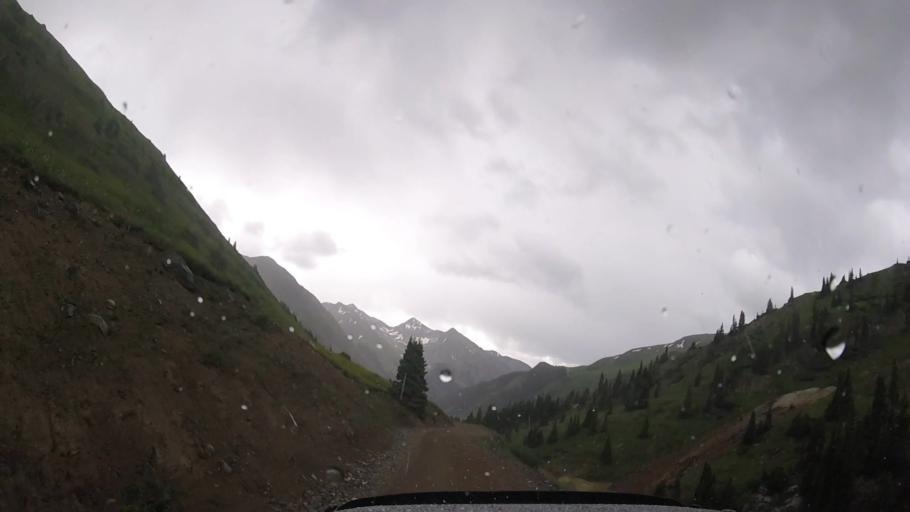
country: US
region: Colorado
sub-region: Ouray County
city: Ouray
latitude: 37.9383
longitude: -107.5727
